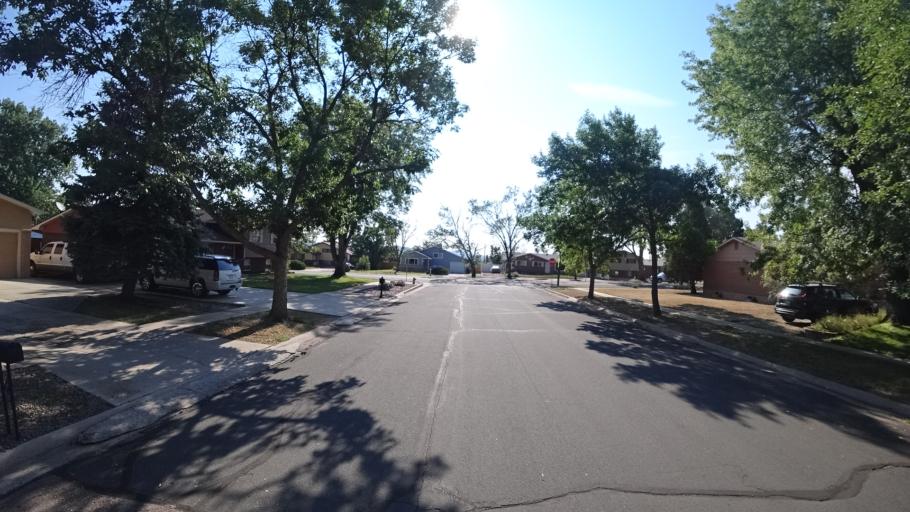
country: US
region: Colorado
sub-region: El Paso County
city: Colorado Springs
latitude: 38.8887
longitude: -104.8360
